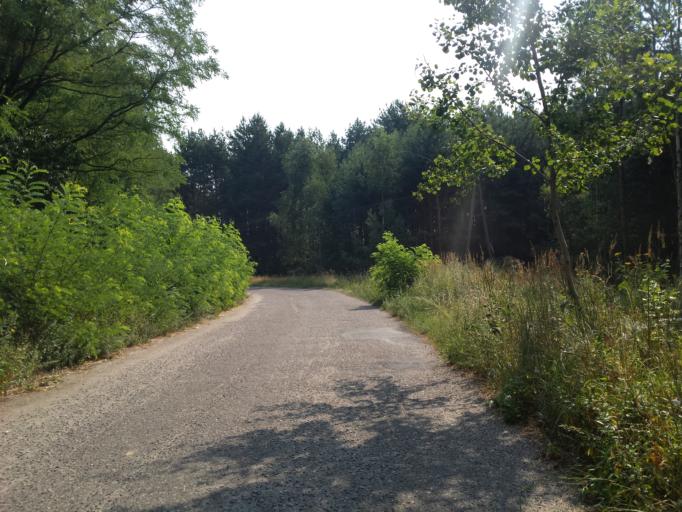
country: PL
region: Greater Poland Voivodeship
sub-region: Powiat czarnkowsko-trzcianecki
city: Polajewo
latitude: 52.7699
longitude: 16.6547
